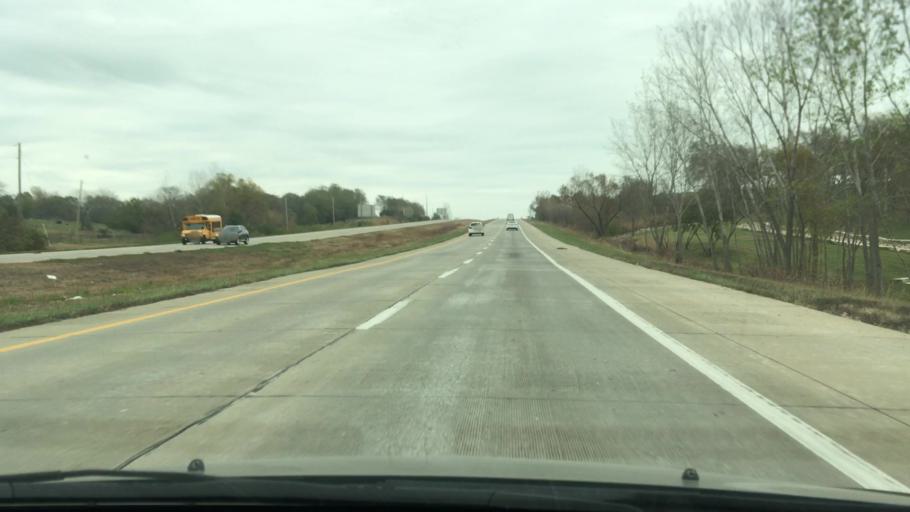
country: US
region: Missouri
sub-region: Jackson County
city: Grandview
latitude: 38.8606
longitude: -94.5751
